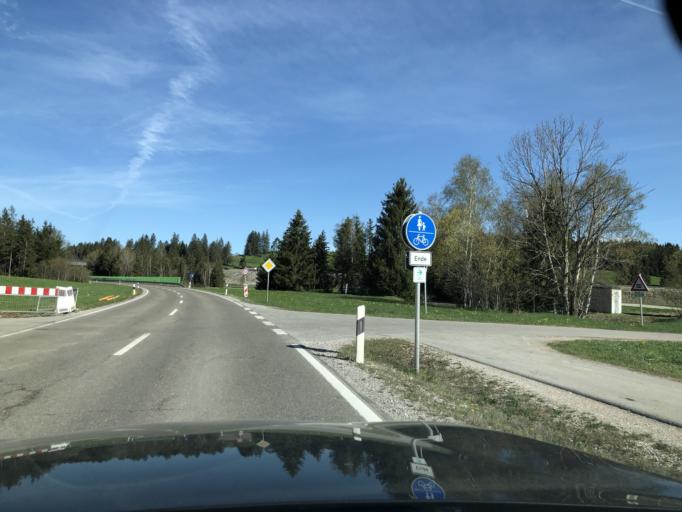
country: DE
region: Bavaria
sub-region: Swabia
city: Eisenberg
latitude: 47.6258
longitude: 10.6056
